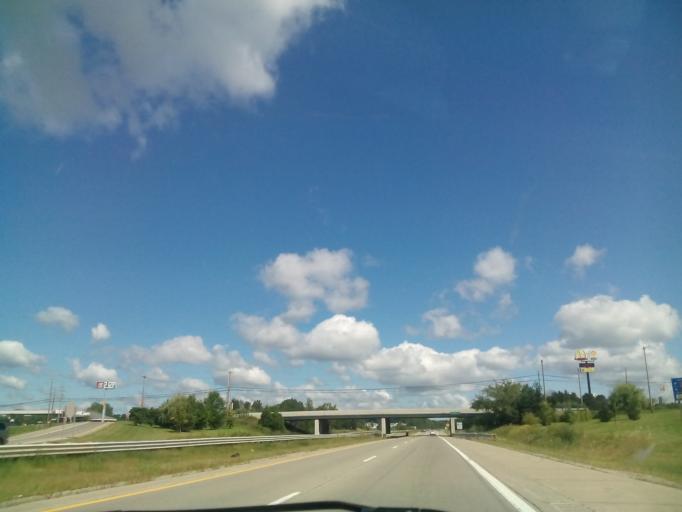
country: US
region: Michigan
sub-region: Genesee County
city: Lake Fenton
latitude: 42.9132
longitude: -83.7258
